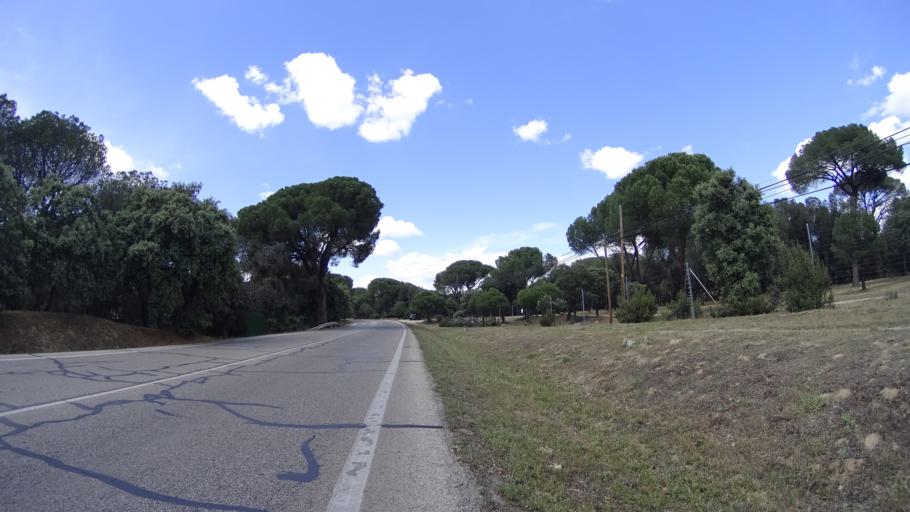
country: ES
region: Madrid
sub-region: Provincia de Madrid
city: Boadilla del Monte
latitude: 40.4316
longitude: -3.8713
